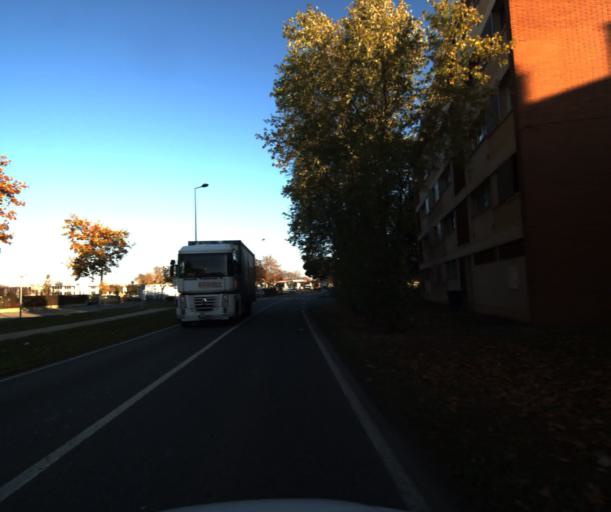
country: FR
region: Midi-Pyrenees
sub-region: Departement de la Haute-Garonne
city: Colomiers
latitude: 43.6099
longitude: 1.3504
